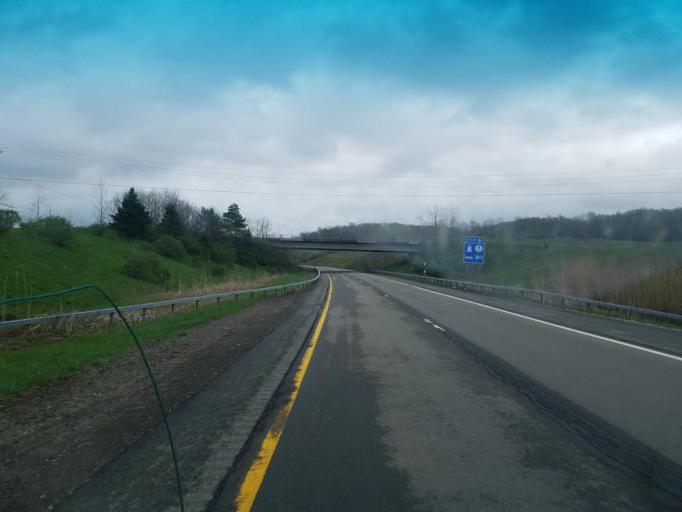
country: US
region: New York
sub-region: Chautauqua County
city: Clymer
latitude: 42.1457
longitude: -79.6103
